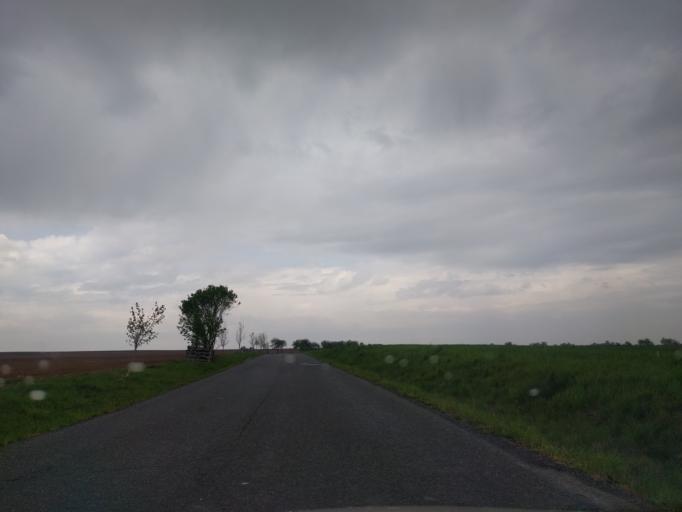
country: CZ
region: Central Bohemia
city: Dobris
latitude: 49.7087
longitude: 14.1477
